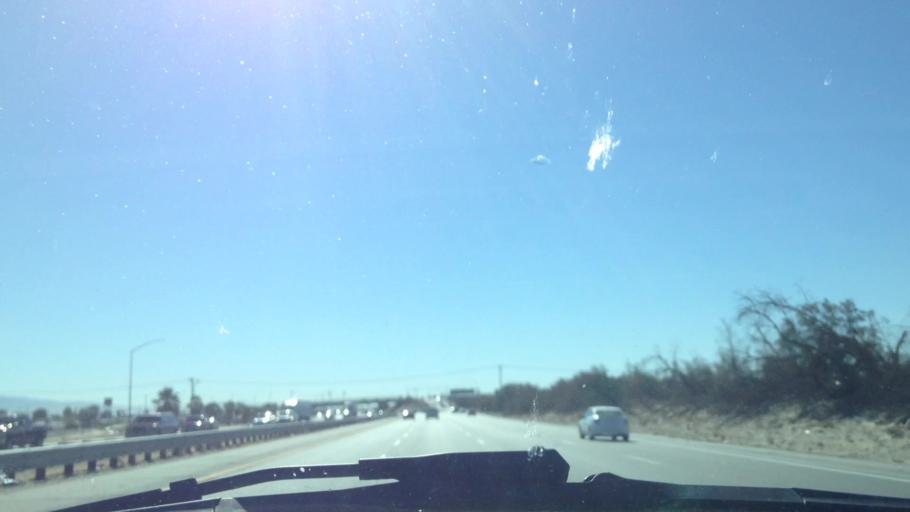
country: US
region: California
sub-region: Riverside County
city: Thousand Palms
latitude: 33.8098
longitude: -116.3910
